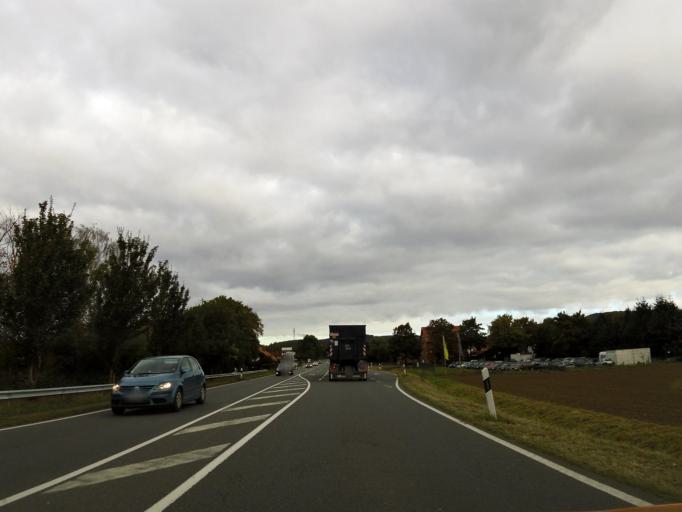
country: DE
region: Lower Saxony
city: Northeim
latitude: 51.7478
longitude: 9.9678
